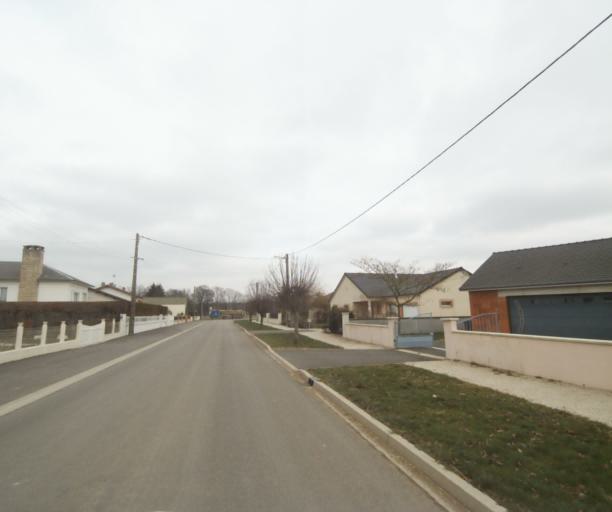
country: FR
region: Champagne-Ardenne
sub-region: Departement de la Haute-Marne
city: Villiers-en-Lieu
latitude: 48.6828
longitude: 4.8779
